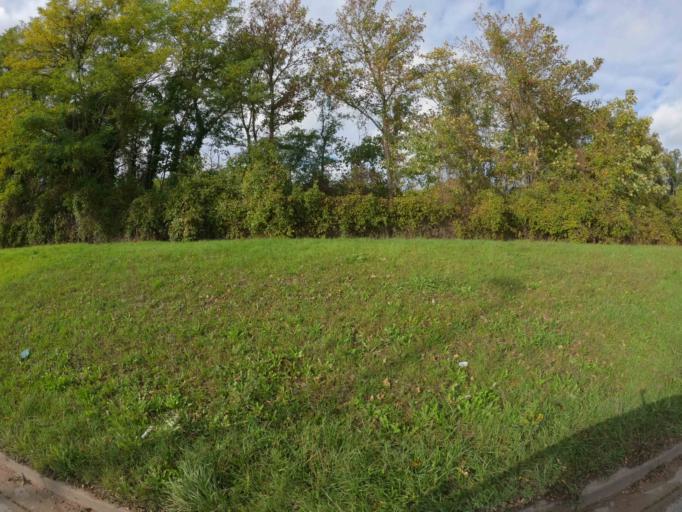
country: FR
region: Ile-de-France
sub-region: Departement de Seine-Saint-Denis
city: Montfermeil
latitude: 48.8949
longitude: 2.5912
